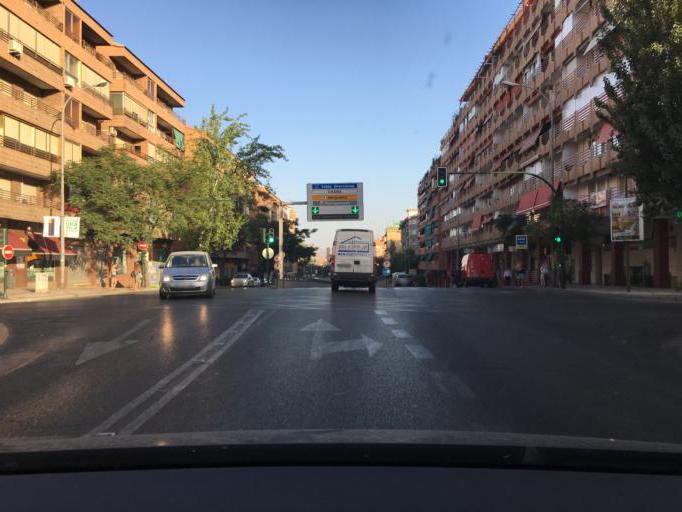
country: ES
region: Andalusia
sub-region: Provincia de Granada
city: Granada
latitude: 37.1882
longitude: -3.6124
